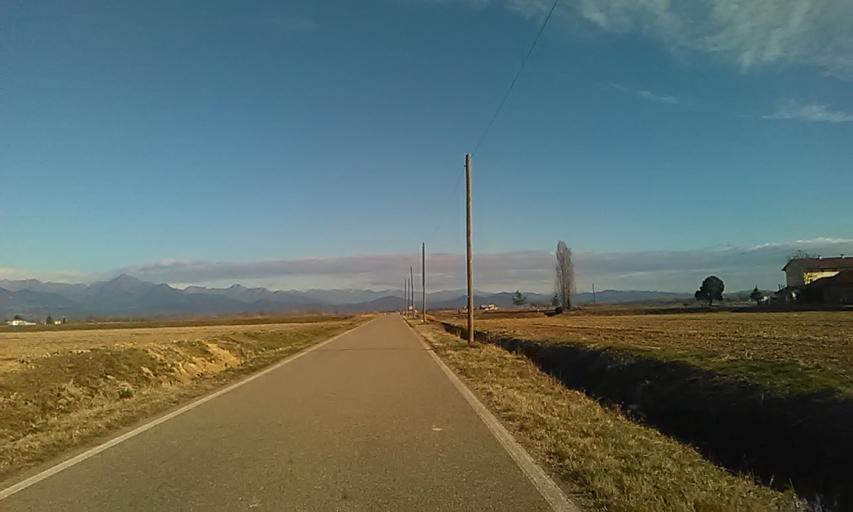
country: IT
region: Piedmont
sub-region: Provincia di Vercelli
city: Buronzo
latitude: 45.5101
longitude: 8.2701
